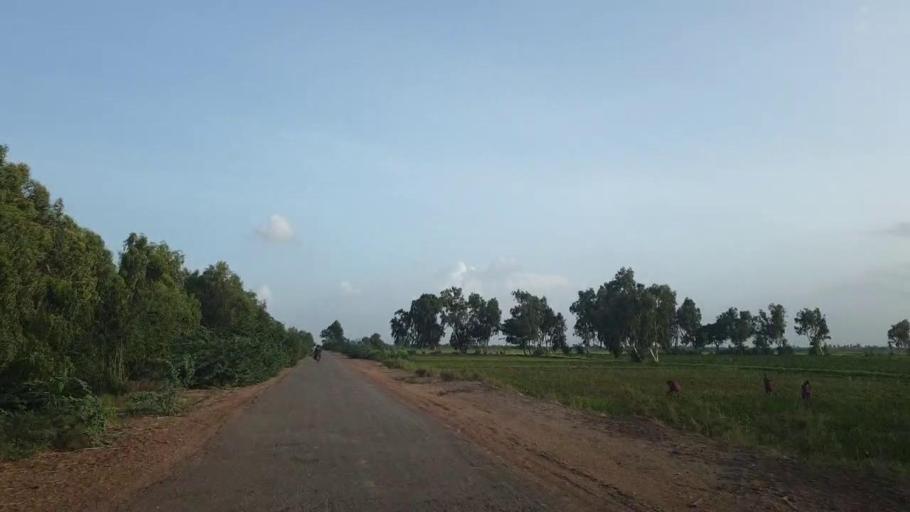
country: PK
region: Sindh
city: Kadhan
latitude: 24.6149
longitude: 69.1158
